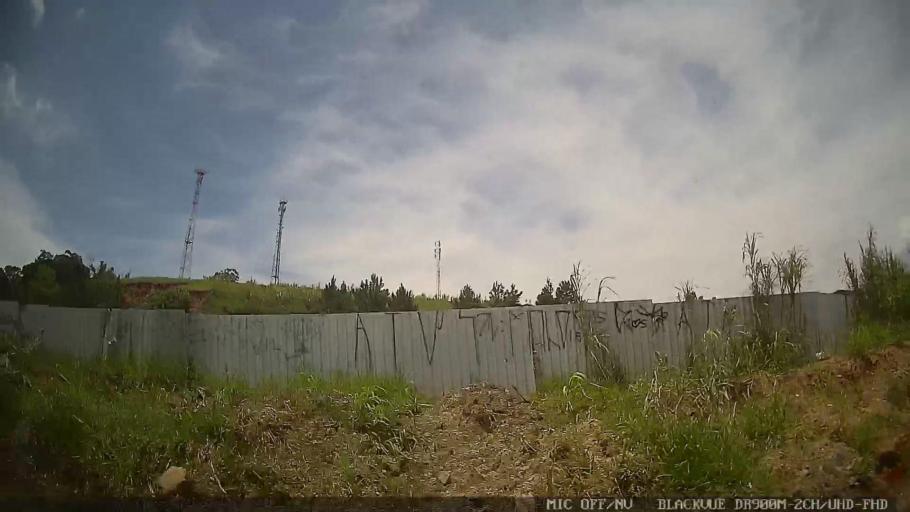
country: BR
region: Sao Paulo
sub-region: Santa Isabel
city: Santa Isabel
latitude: -23.3418
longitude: -46.2077
